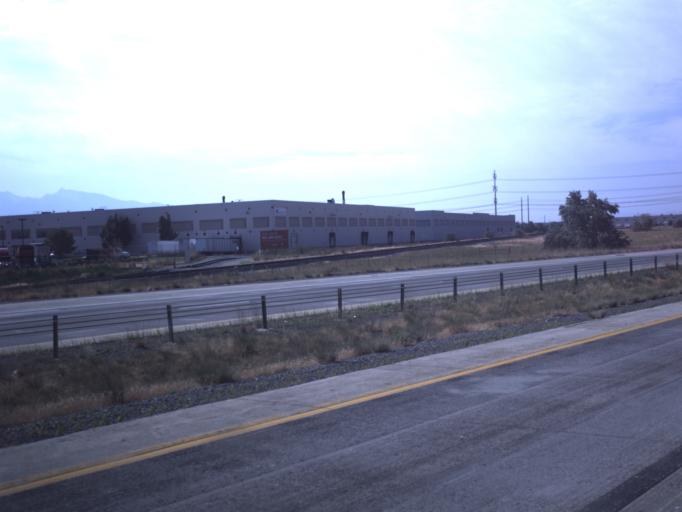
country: US
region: Utah
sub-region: Salt Lake County
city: West Valley City
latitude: 40.7486
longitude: -111.9875
